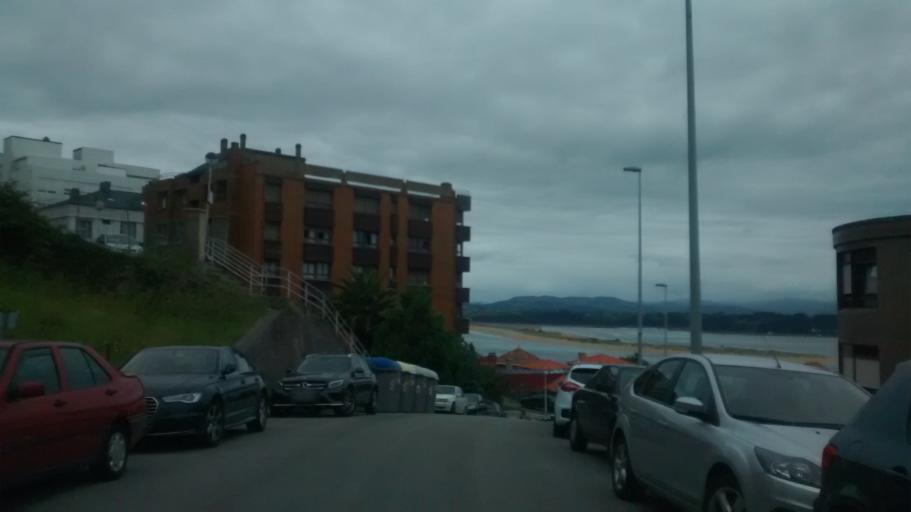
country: ES
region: Cantabria
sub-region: Provincia de Cantabria
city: Santander
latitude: 43.4648
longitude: -3.7866
